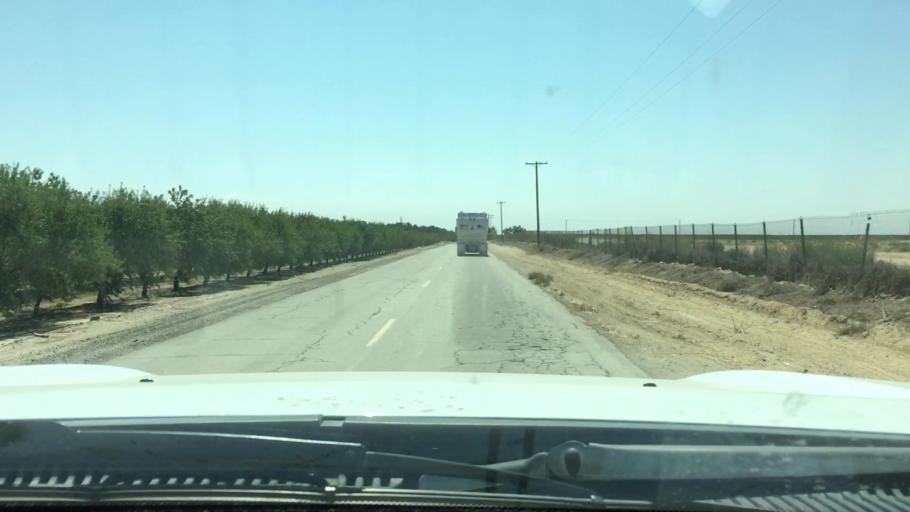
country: US
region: California
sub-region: Kern County
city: Wasco
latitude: 35.5109
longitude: -119.4033
